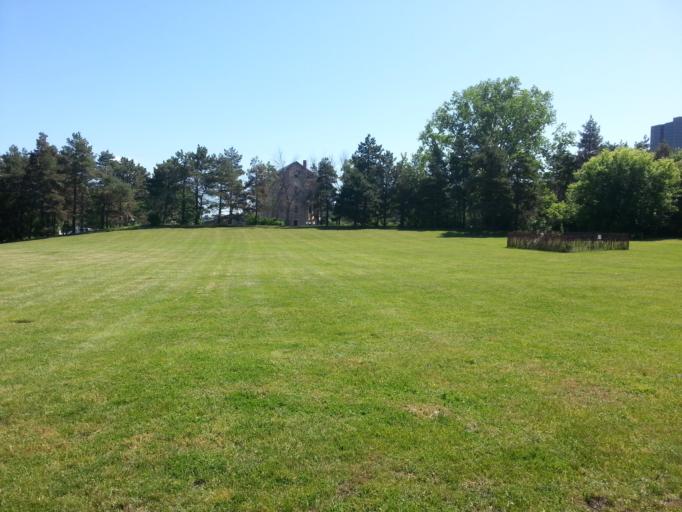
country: CA
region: Ontario
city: Ottawa
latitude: 45.4208
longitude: -75.7143
